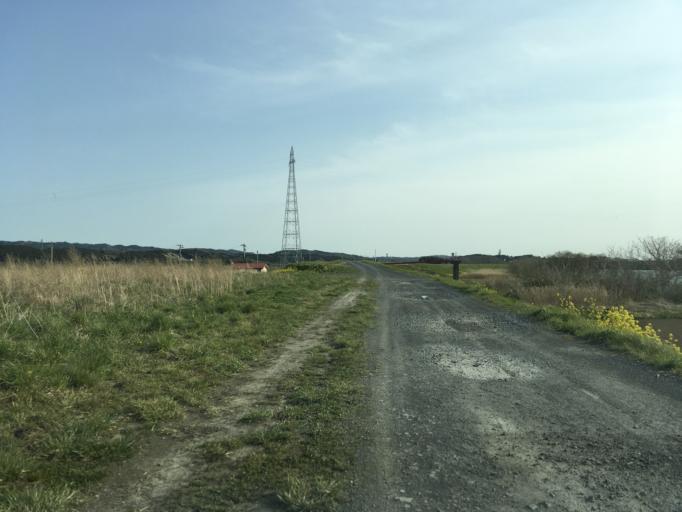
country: JP
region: Miyagi
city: Wakuya
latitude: 38.7199
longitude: 141.2703
